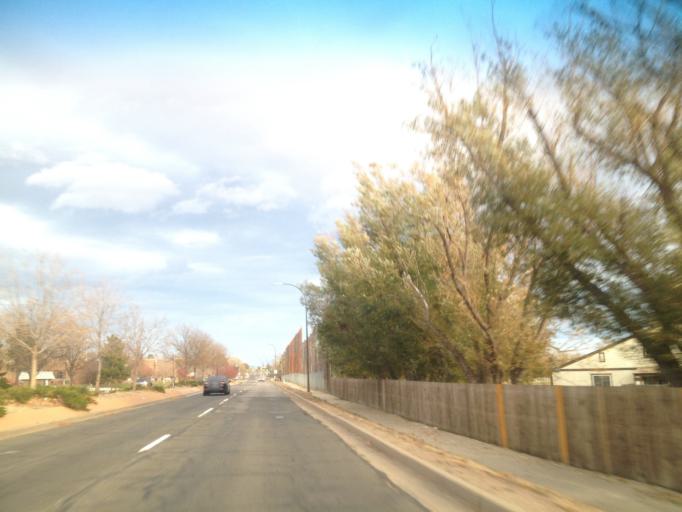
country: US
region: Colorado
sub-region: Adams County
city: Westminster
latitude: 39.8565
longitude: -105.0715
